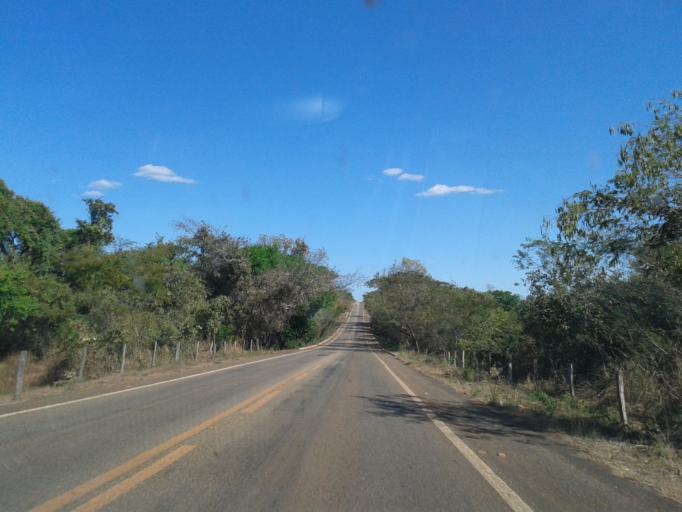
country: BR
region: Goias
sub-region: Crixas
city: Crixas
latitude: -14.0359
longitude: -50.3285
